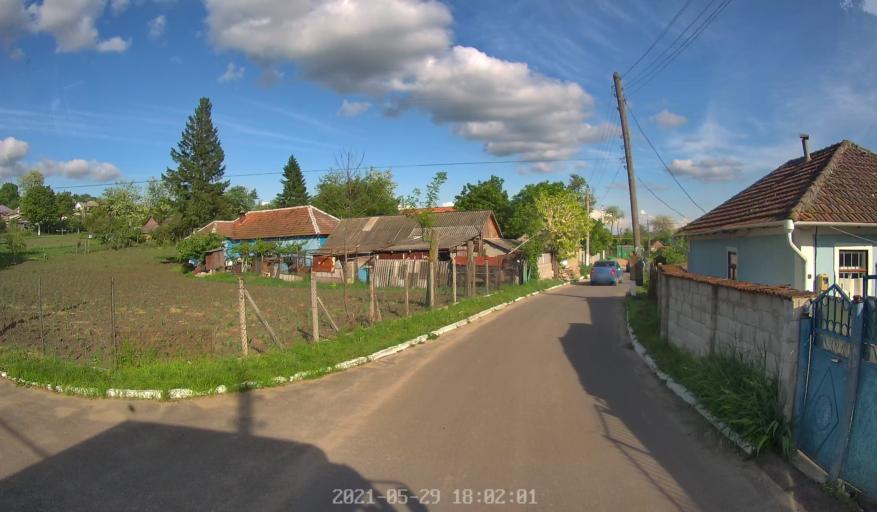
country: MD
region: Laloveni
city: Ialoveni
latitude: 46.8362
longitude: 28.8508
